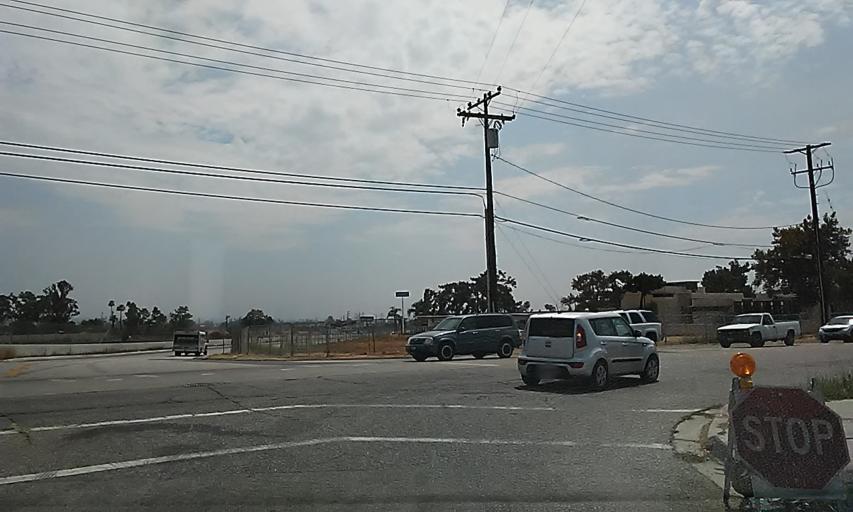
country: US
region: California
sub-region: San Bernardino County
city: Grand Terrace
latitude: 34.0340
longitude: -117.3259
